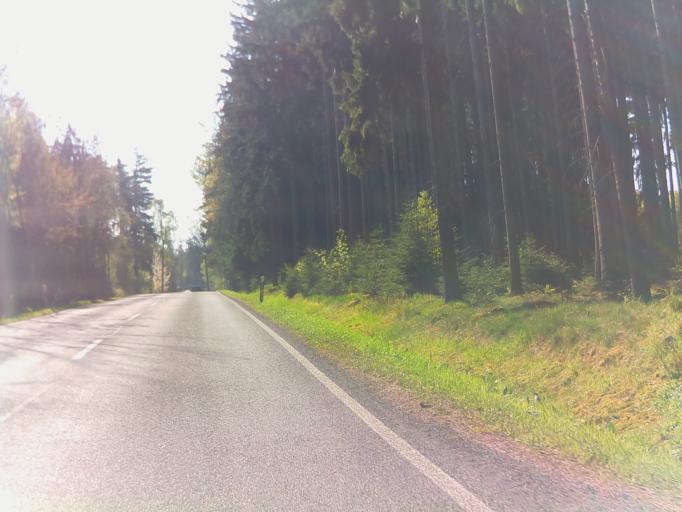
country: DE
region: Thuringia
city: Dittersdorf
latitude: 50.6652
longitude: 11.8007
